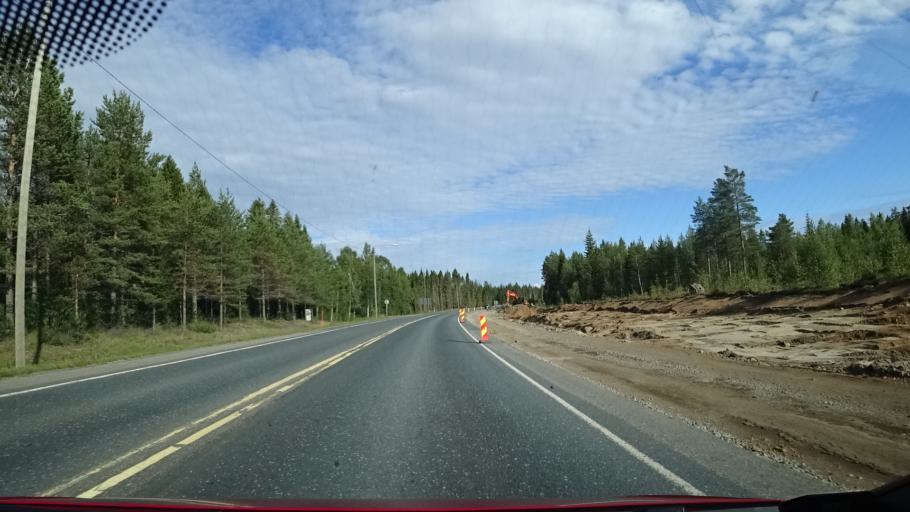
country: FI
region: Lapland
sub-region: Kemi-Tornio
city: Simo
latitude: 65.6566
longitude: 25.0828
